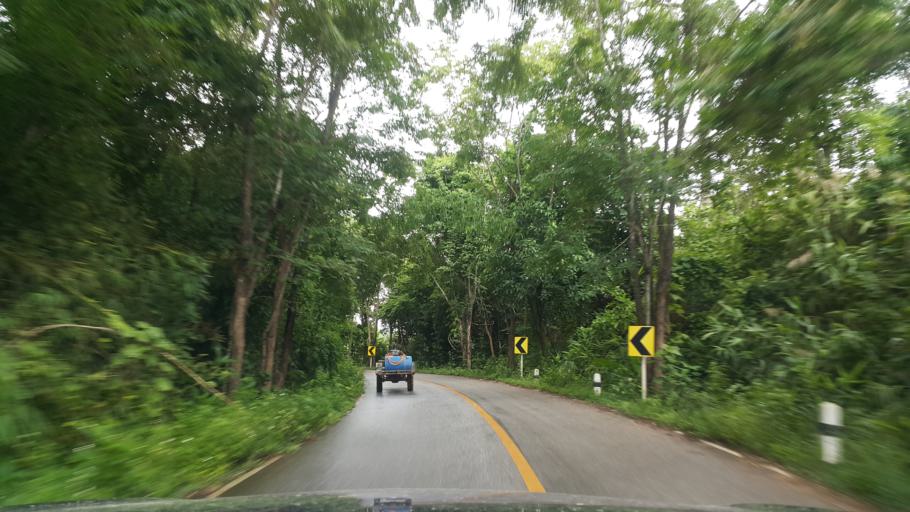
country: TH
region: Loei
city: Na Haeo
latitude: 17.4843
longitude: 100.8057
